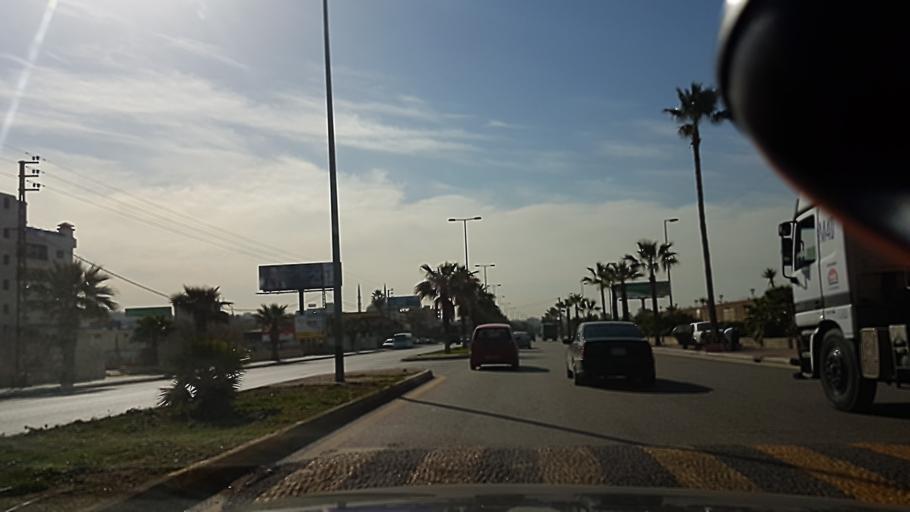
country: LB
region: Liban-Sud
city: Sidon
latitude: 33.5857
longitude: 35.3861
